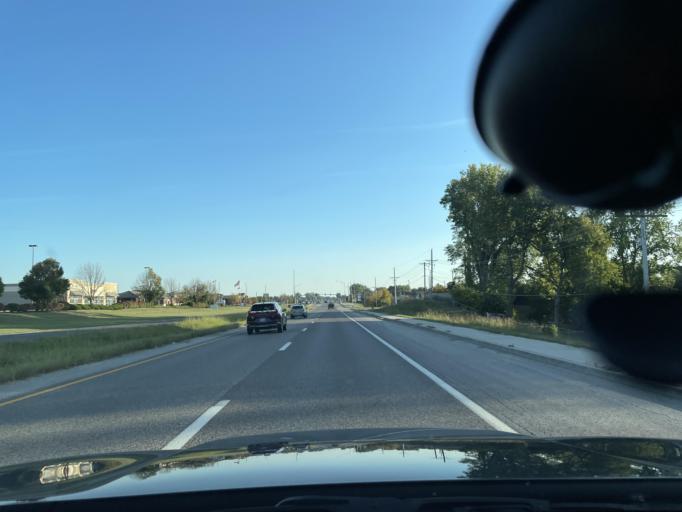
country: US
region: Missouri
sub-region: Andrew County
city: Country Club Village
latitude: 39.8171
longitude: -94.8153
